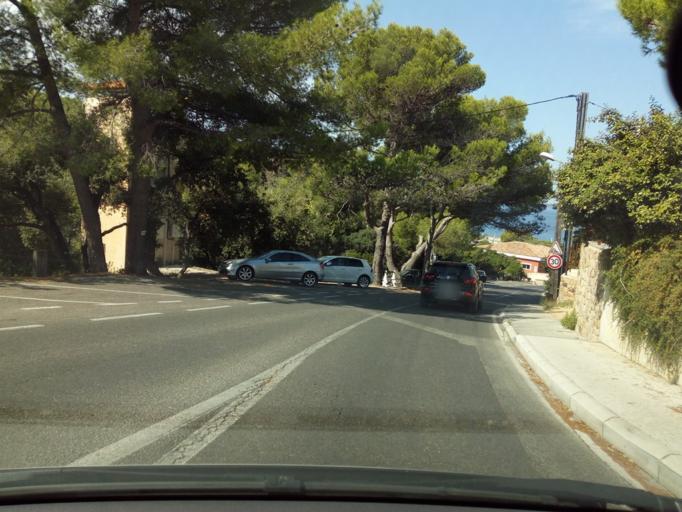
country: FR
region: Provence-Alpes-Cote d'Azur
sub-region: Departement du Var
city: Le Pradet
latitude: 43.0843
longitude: 6.0234
